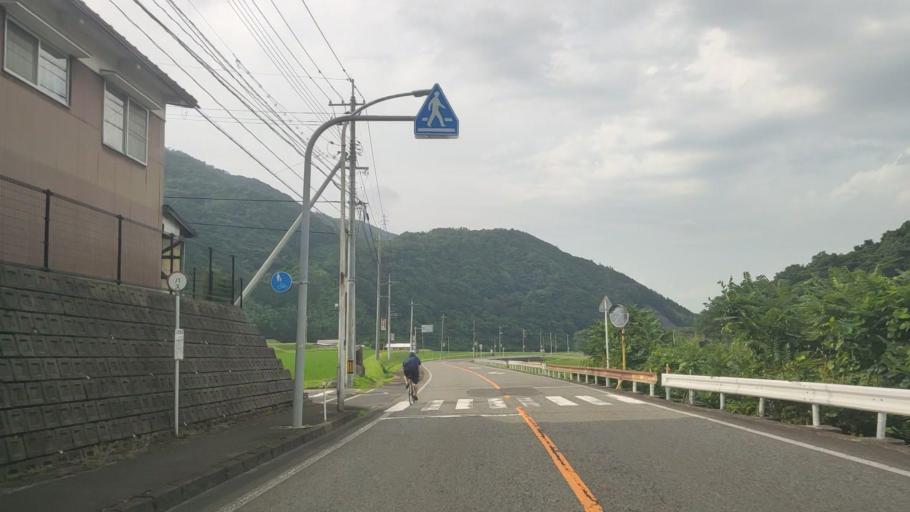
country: JP
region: Tottori
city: Kurayoshi
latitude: 35.3582
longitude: 133.8460
